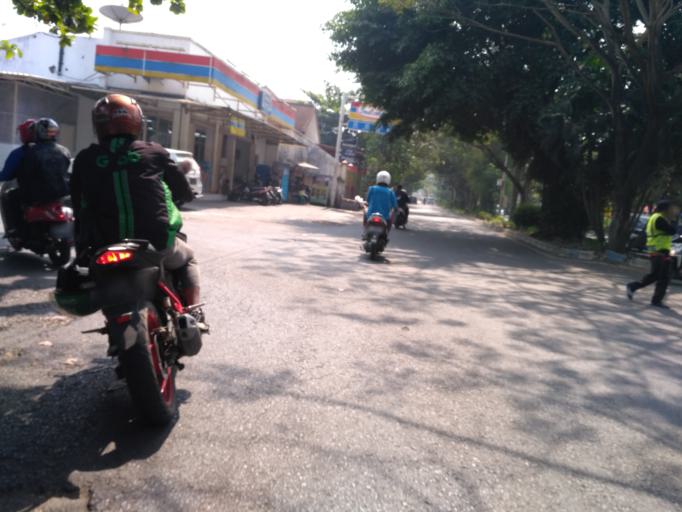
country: ID
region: East Java
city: Malang
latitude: -7.9728
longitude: 112.6631
